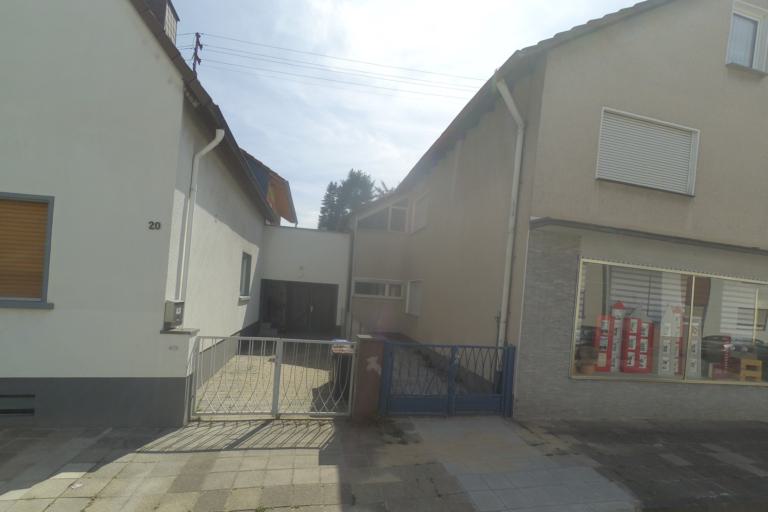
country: DE
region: Rheinland-Pfalz
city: Limburgerhof
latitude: 49.4233
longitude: 8.3856
